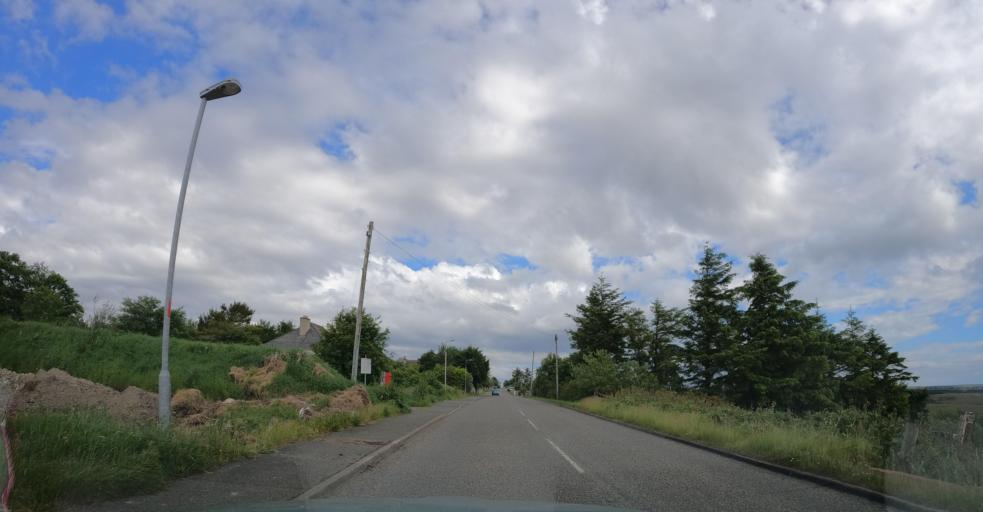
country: GB
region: Scotland
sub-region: Eilean Siar
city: Isle of Lewis
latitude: 58.2413
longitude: -6.3900
